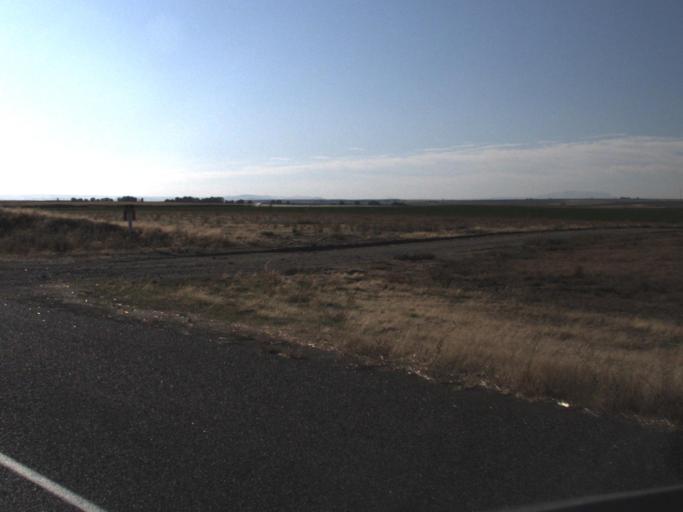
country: US
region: Washington
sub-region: Walla Walla County
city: Burbank
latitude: 46.2627
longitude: -118.7869
